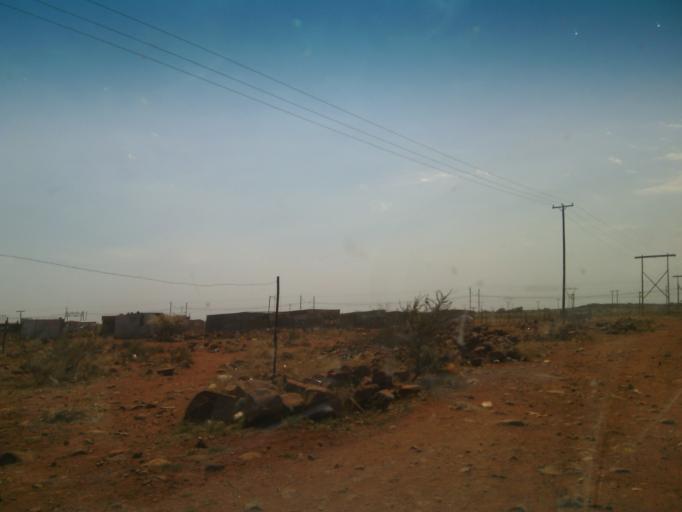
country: ZA
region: Northern Cape
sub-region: Frances Baard District Municipality
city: Barkly West
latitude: -28.5195
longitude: 24.4986
